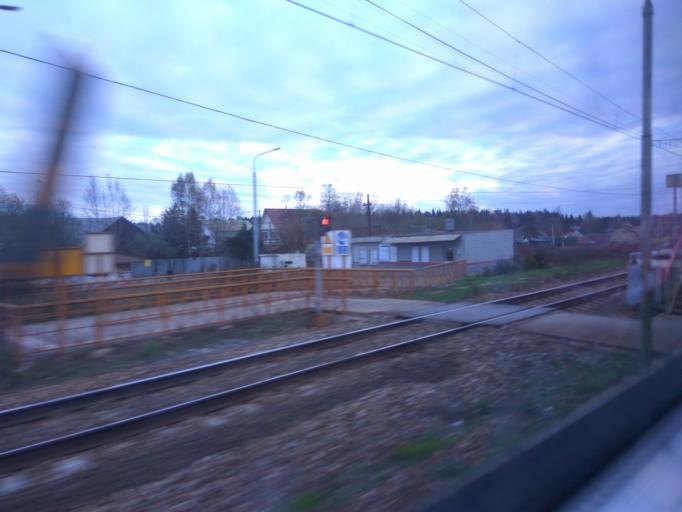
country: RU
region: Moskovskaya
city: Selyatino
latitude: 55.4810
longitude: 36.9178
